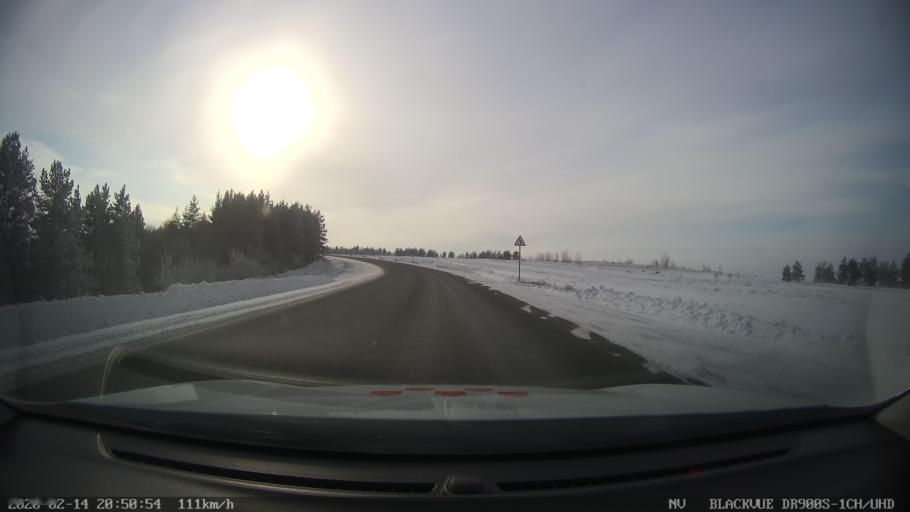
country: RU
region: Tatarstan
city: Kuybyshevskiy Zaton
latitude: 55.2199
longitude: 49.2323
